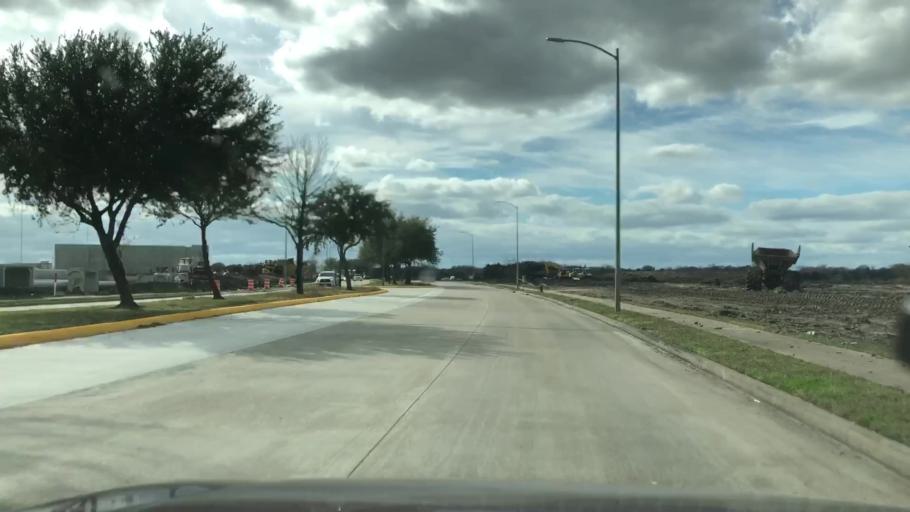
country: US
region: Texas
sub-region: Fort Bend County
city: Missouri City
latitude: 29.6120
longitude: -95.4688
